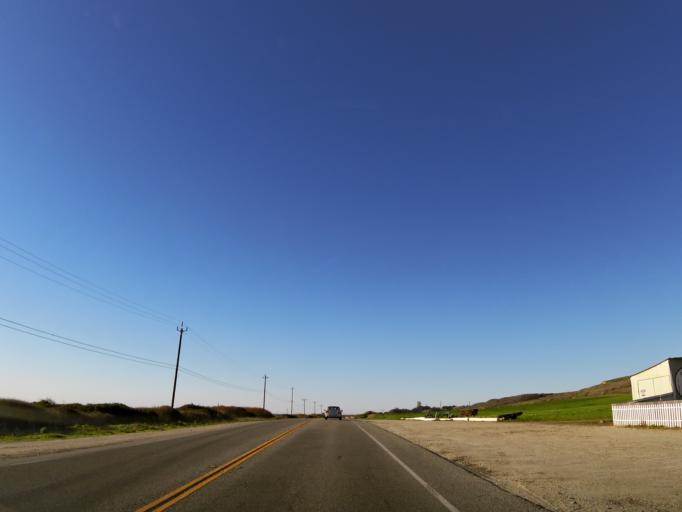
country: US
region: California
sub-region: Santa Cruz County
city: Bonny Doon
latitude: 36.9959
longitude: -122.1731
